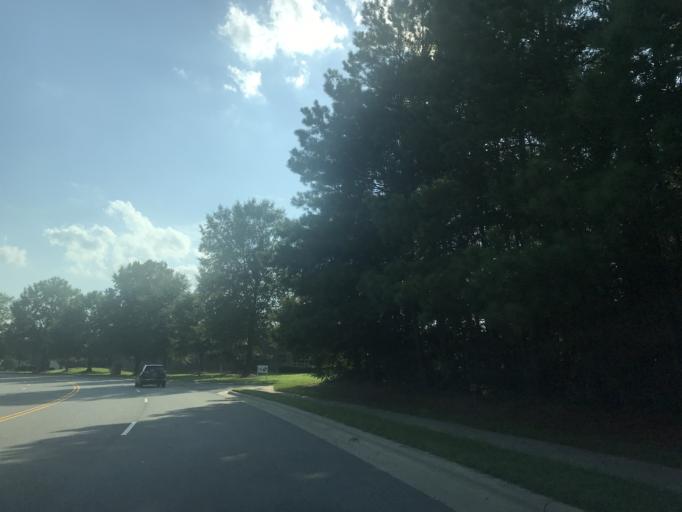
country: US
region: North Carolina
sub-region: Wake County
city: Knightdale
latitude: 35.7723
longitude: -78.5554
